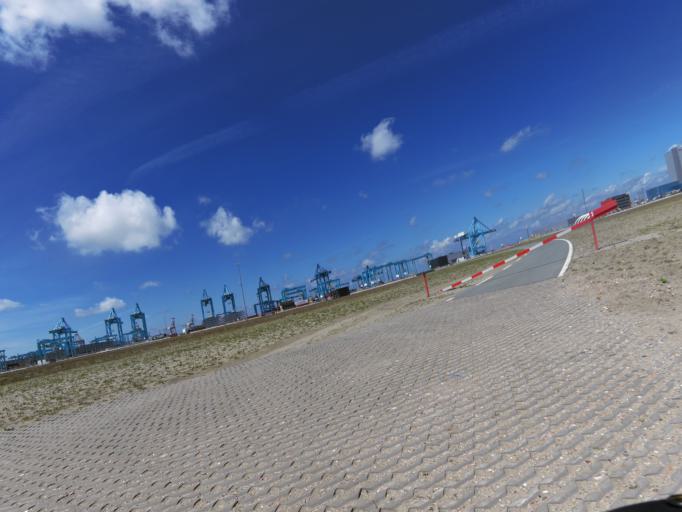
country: NL
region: South Holland
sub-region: Gemeente Rotterdam
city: Hoek van Holland
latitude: 51.9502
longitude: 4.0137
